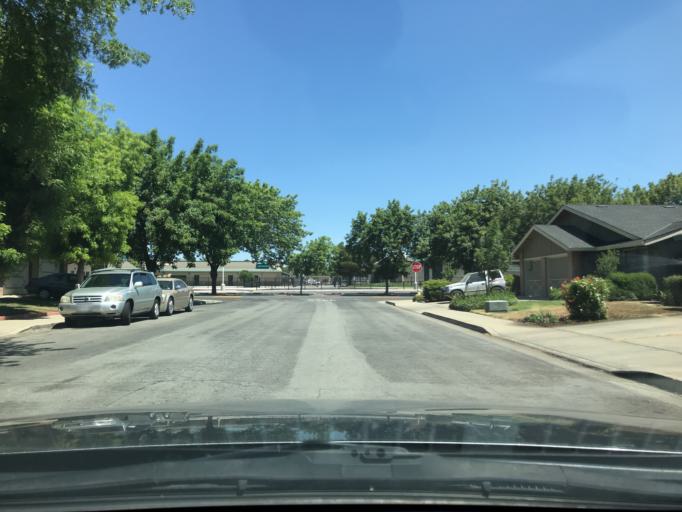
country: US
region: California
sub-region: Merced County
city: Merced
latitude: 37.3258
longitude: -120.4850
